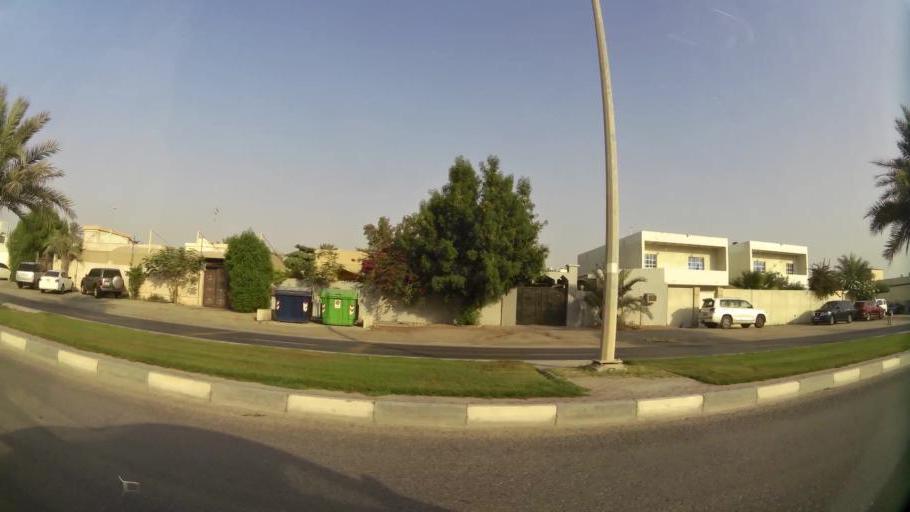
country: AE
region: Ajman
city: Ajman
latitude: 25.3770
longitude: 55.4335
